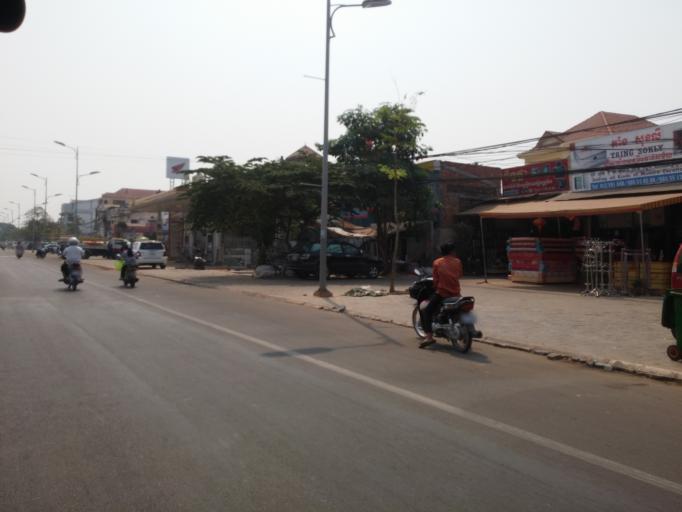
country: KH
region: Siem Reap
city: Siem Reap
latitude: 13.3605
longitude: 103.8640
